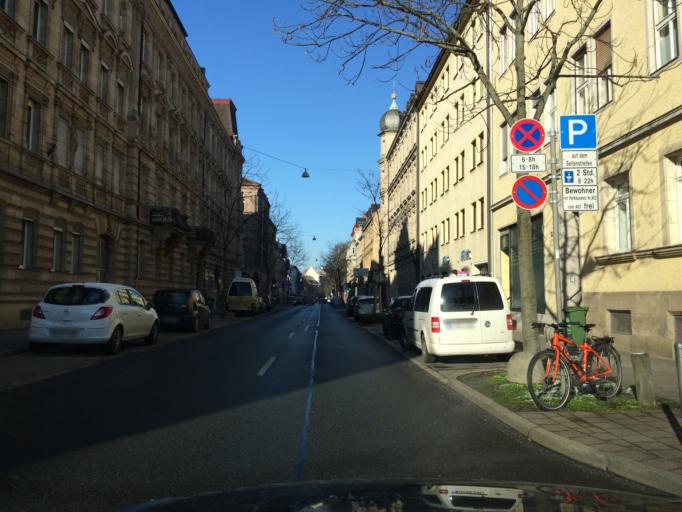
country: DE
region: Bavaria
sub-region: Regierungsbezirk Mittelfranken
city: Furth
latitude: 49.4705
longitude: 10.9985
